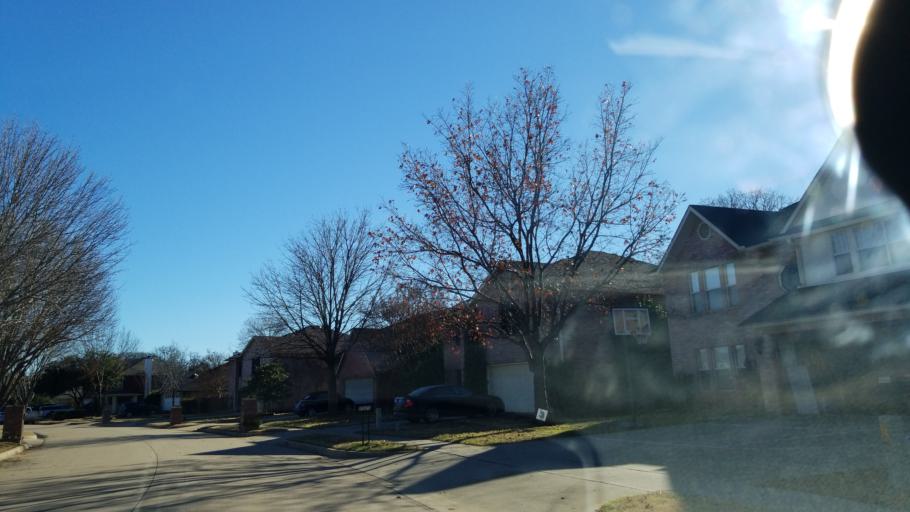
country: US
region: Texas
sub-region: Denton County
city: Corinth
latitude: 33.1385
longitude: -97.0806
